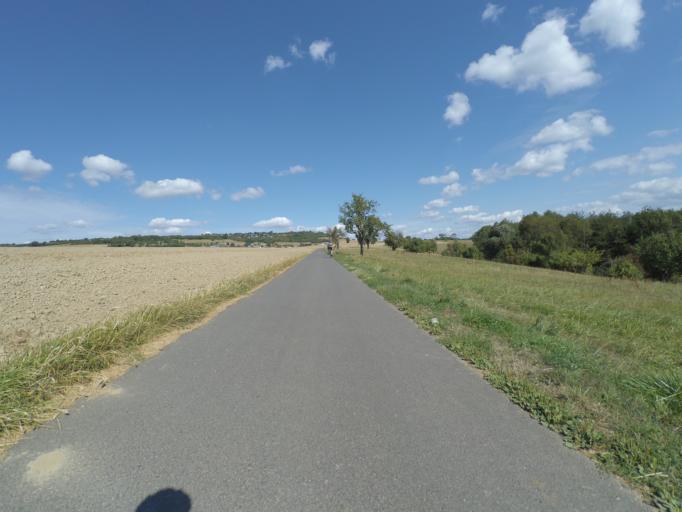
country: DE
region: Rheinland-Pfalz
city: Trassem
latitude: 49.5881
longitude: 6.5113
